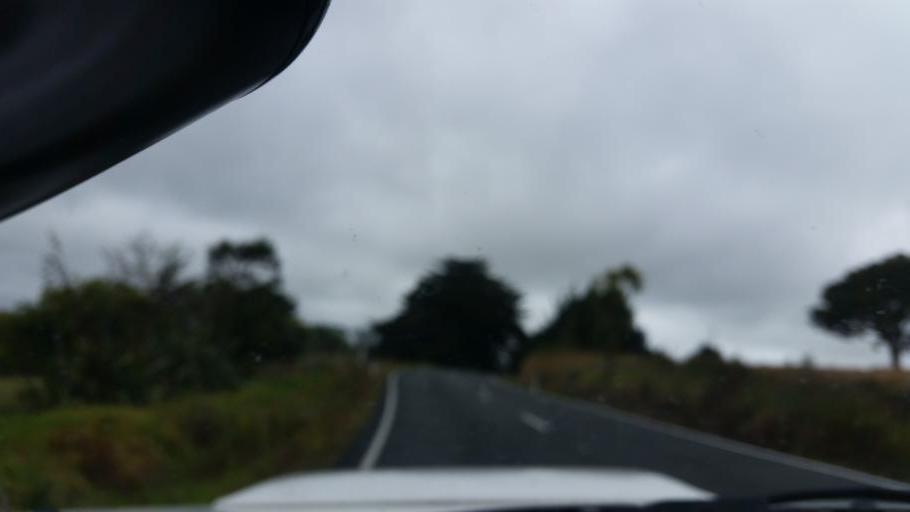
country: NZ
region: Auckland
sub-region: Auckland
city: Wellsford
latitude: -36.1459
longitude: 174.4809
